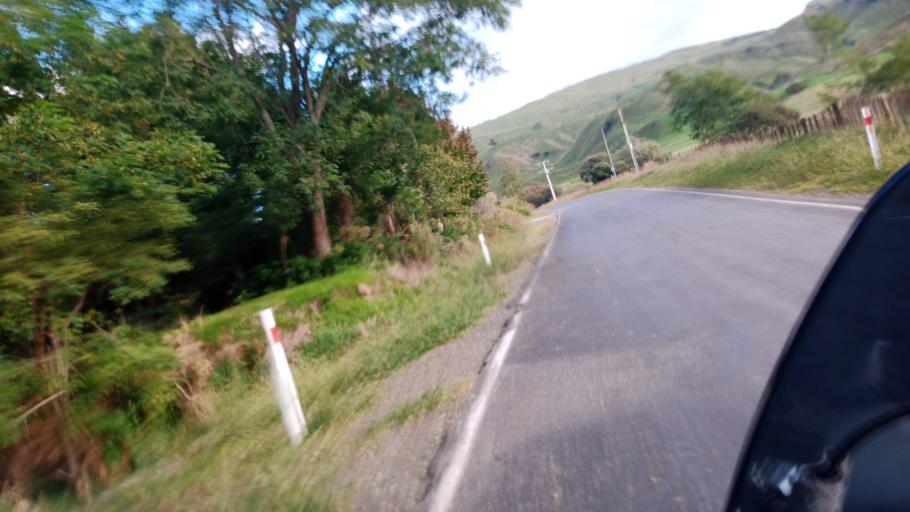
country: NZ
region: Gisborne
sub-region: Gisborne District
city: Gisborne
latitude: -38.5399
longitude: 177.5863
